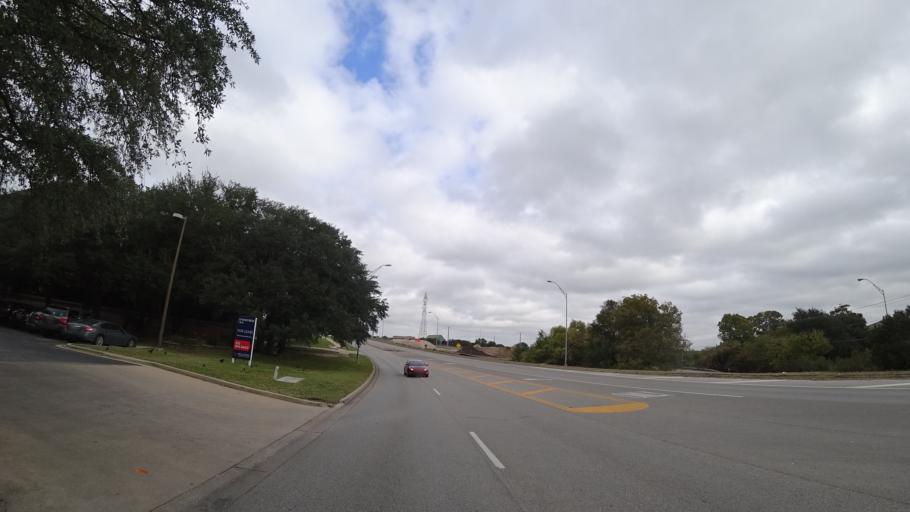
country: US
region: Texas
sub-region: Travis County
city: Wells Branch
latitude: 30.4060
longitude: -97.7157
